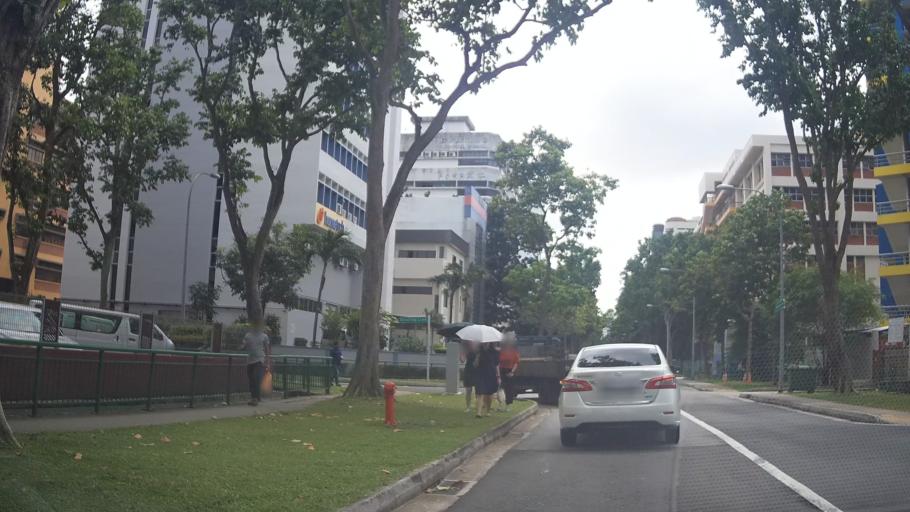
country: SG
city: Singapore
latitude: 1.3284
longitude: 103.8736
